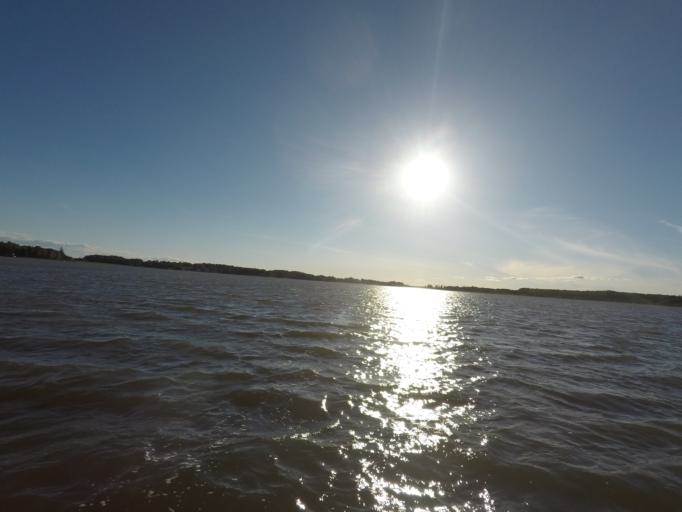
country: SE
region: Vaestmanland
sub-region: Vasteras
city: Vasteras
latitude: 59.5206
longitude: 16.5589
